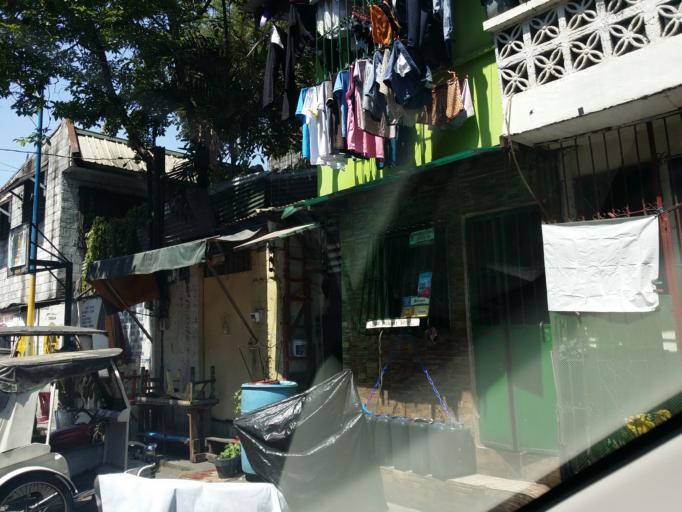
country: PH
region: Metro Manila
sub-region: Mandaluyong
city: Mandaluyong City
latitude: 14.5854
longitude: 121.0321
